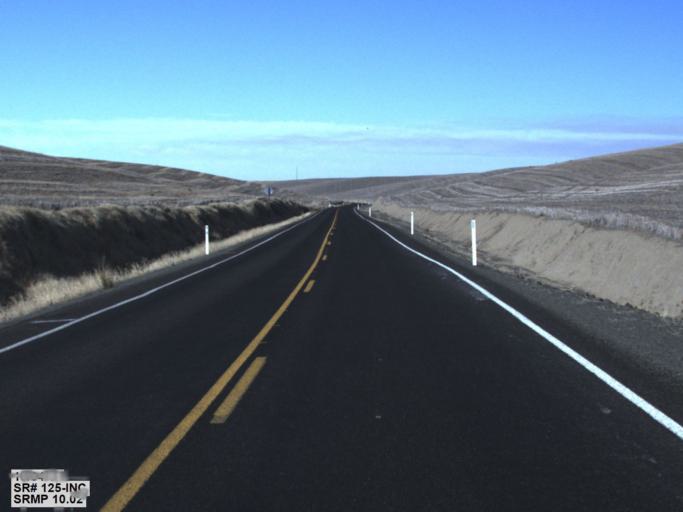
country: US
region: Washington
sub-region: Walla Walla County
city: Walla Walla
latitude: 46.1179
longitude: -118.3723
